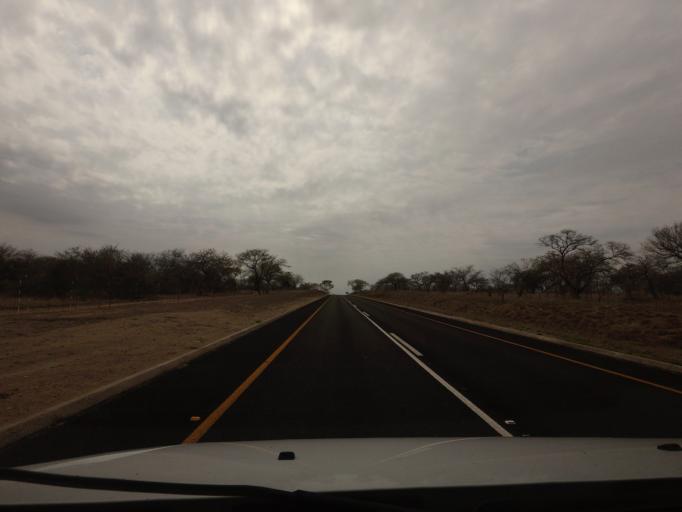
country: ZA
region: Limpopo
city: Thulamahashi
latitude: -24.5560
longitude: 31.2236
